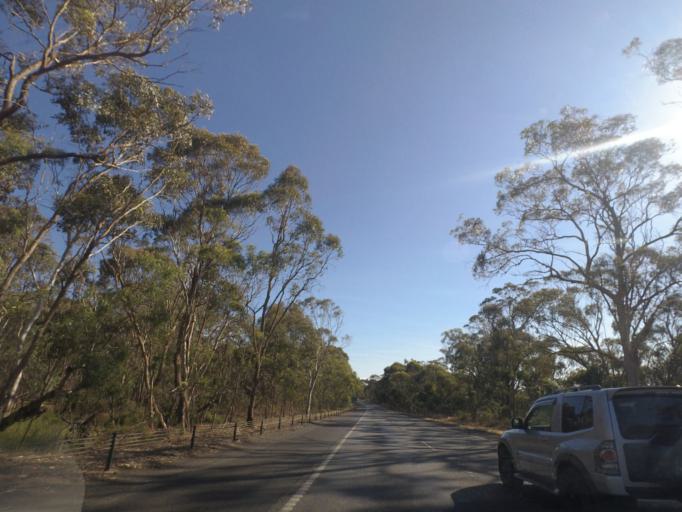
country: AU
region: Victoria
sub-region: Murrindindi
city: Kinglake West
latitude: -37.1761
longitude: 145.0722
